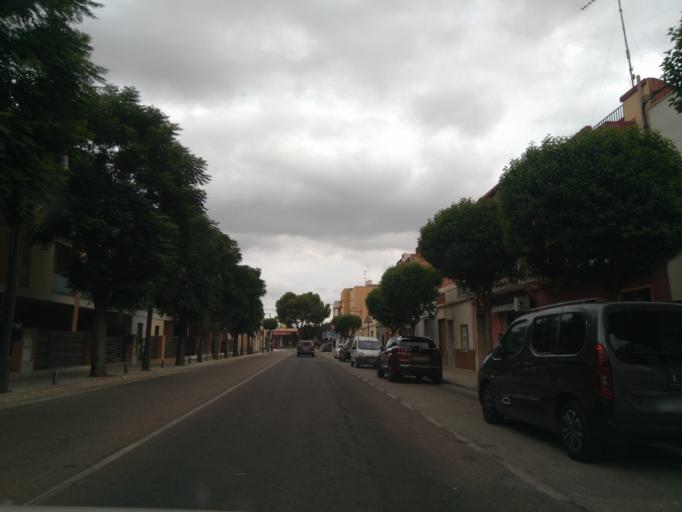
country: ES
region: Valencia
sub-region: Provincia de Valencia
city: L'Alcudia
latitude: 39.2005
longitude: -0.5054
